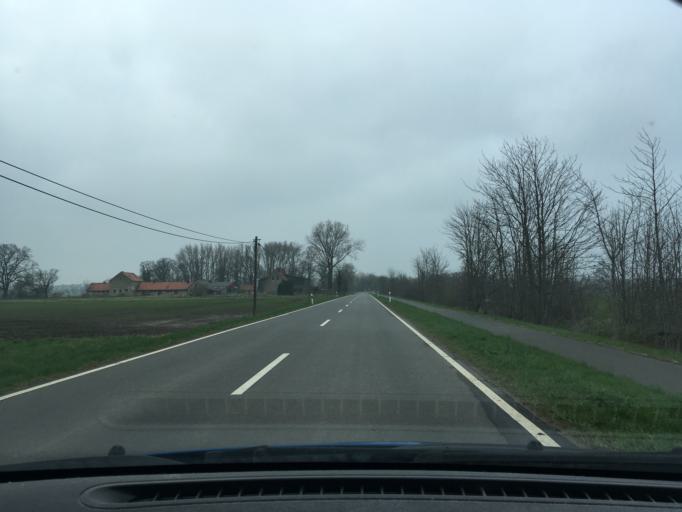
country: DE
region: Lower Saxony
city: Neu Darchau
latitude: 53.2967
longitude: 10.8859
